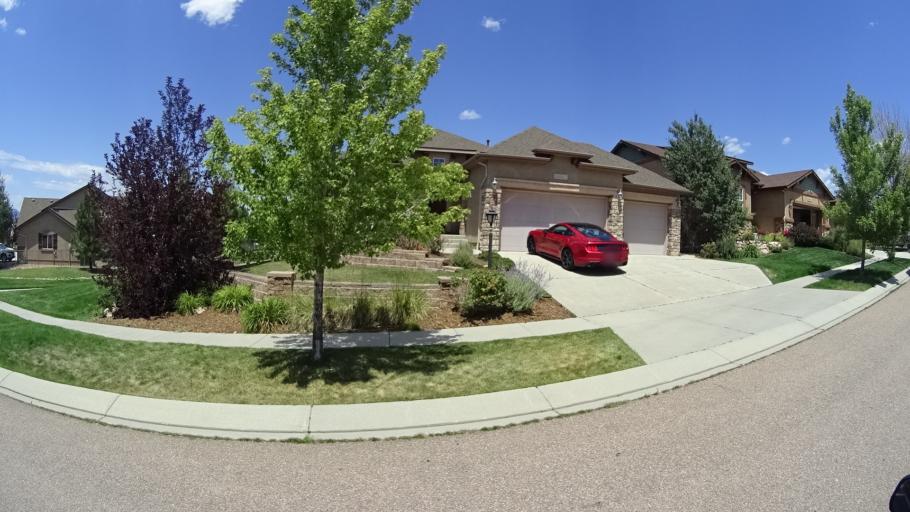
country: US
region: Colorado
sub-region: El Paso County
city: Black Forest
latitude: 38.9683
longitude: -104.7603
